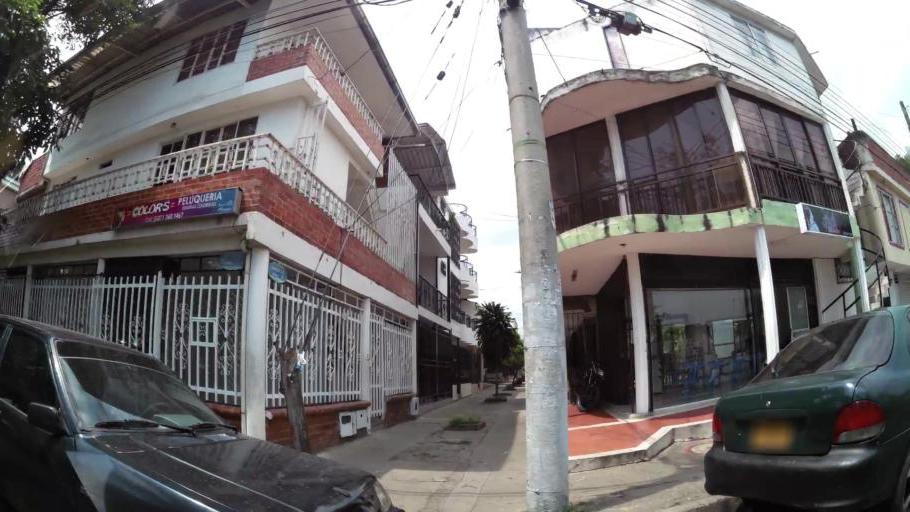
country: CO
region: Valle del Cauca
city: Cali
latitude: 3.4747
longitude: -76.4955
